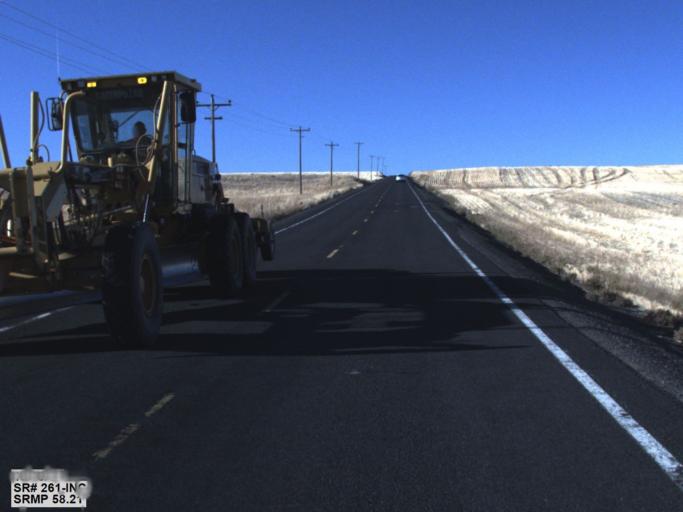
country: US
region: Washington
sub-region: Adams County
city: Ritzville
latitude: 47.0517
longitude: -118.3576
